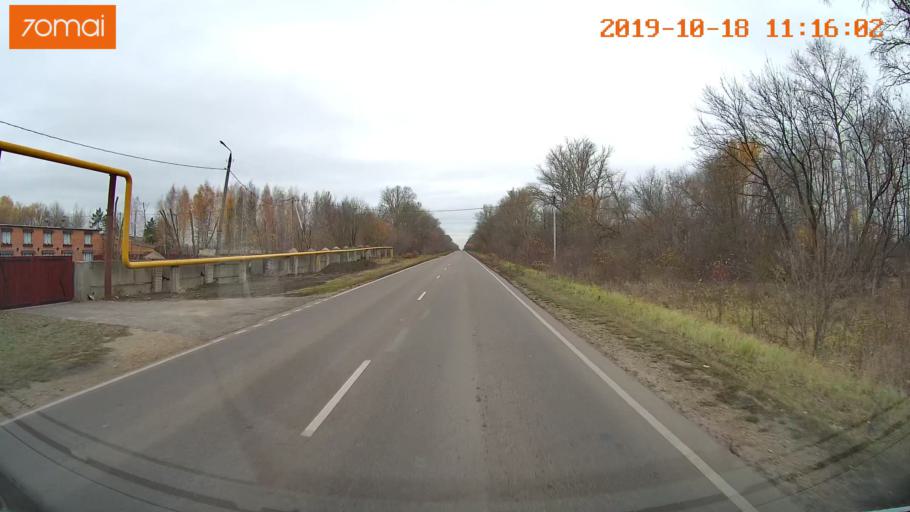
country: RU
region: Tula
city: Kimovsk
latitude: 54.0013
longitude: 38.5481
